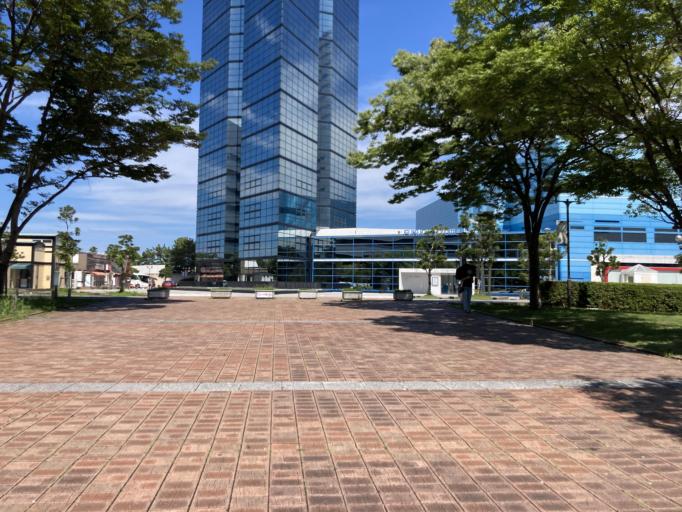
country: JP
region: Fukuoka
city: Fukuoka-shi
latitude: 33.5926
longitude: 130.3516
